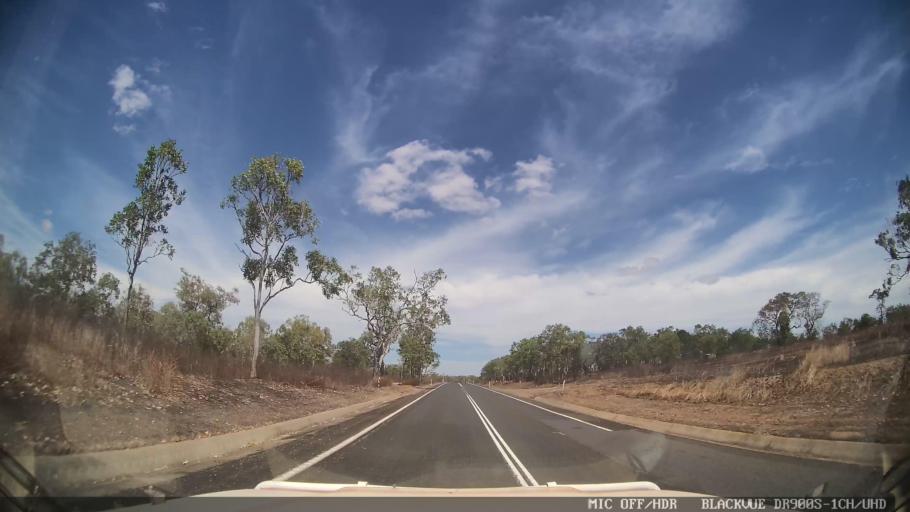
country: AU
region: Queensland
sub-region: Cook
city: Cooktown
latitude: -15.8052
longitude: 144.9210
